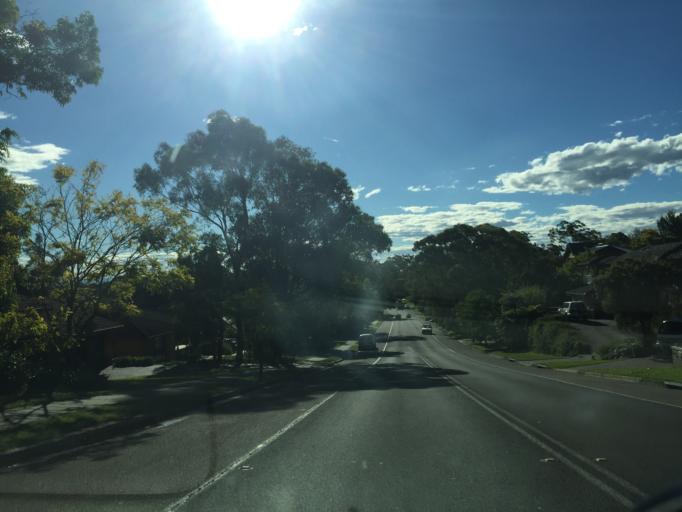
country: AU
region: New South Wales
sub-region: The Hills Shire
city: Glenhaven
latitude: -33.6971
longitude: 150.9991
